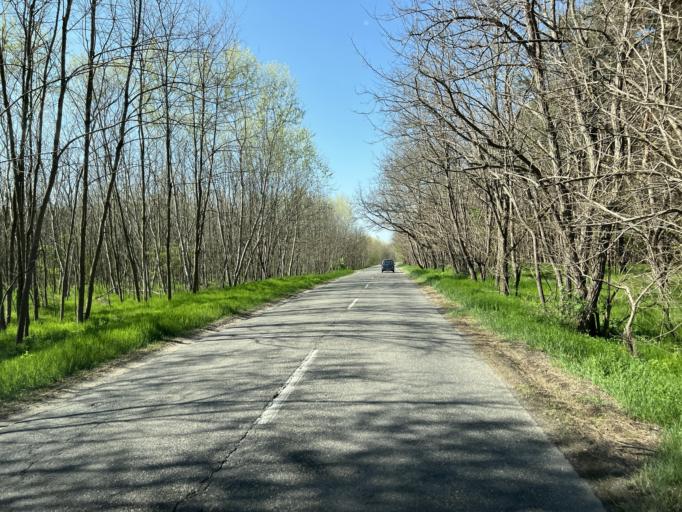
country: HU
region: Pest
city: Felsopakony
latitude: 47.3472
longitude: 19.2480
